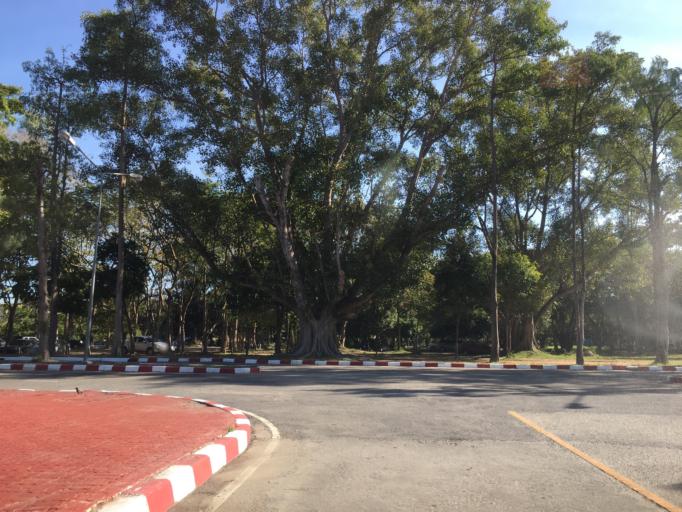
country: TH
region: Chiang Mai
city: Chiang Mai
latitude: 18.8387
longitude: 98.9720
